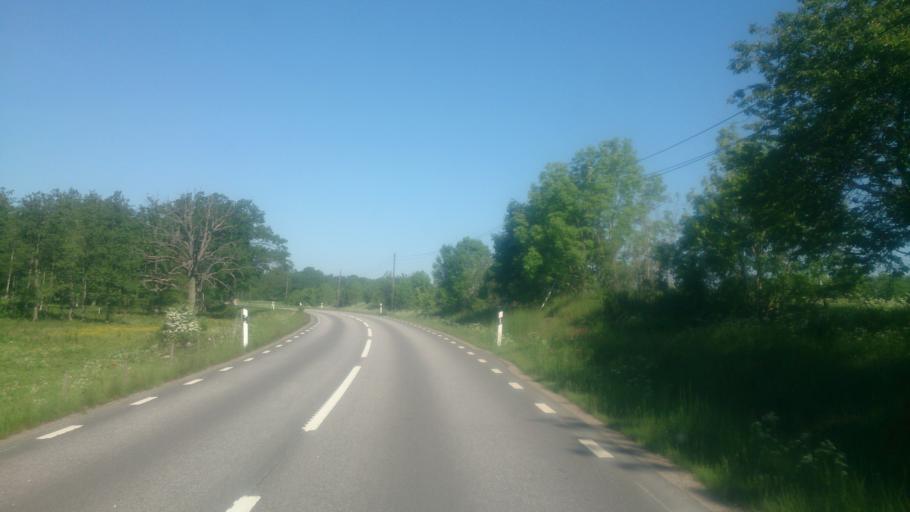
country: SE
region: OEstergoetland
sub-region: Atvidabergs Kommun
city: Atvidaberg
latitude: 58.1390
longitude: 16.0880
